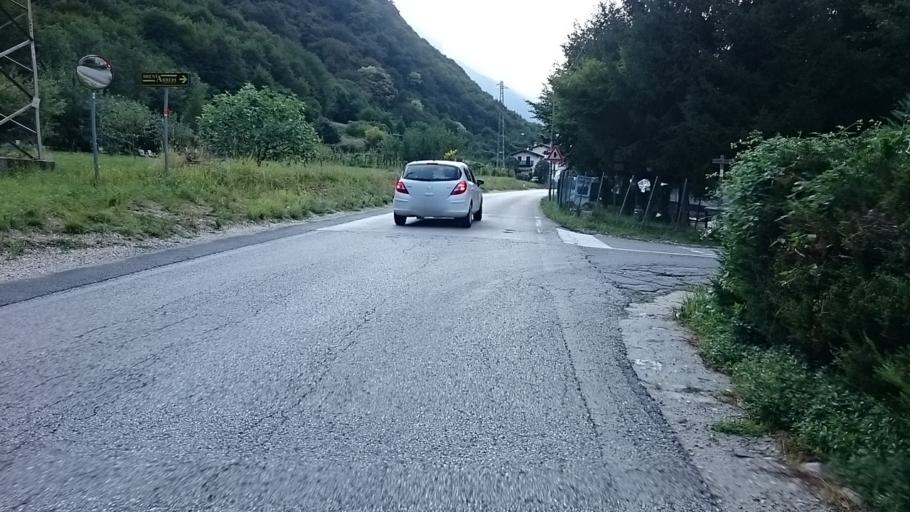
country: IT
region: Veneto
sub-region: Provincia di Vicenza
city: San Nazario
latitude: 45.8347
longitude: 11.6920
